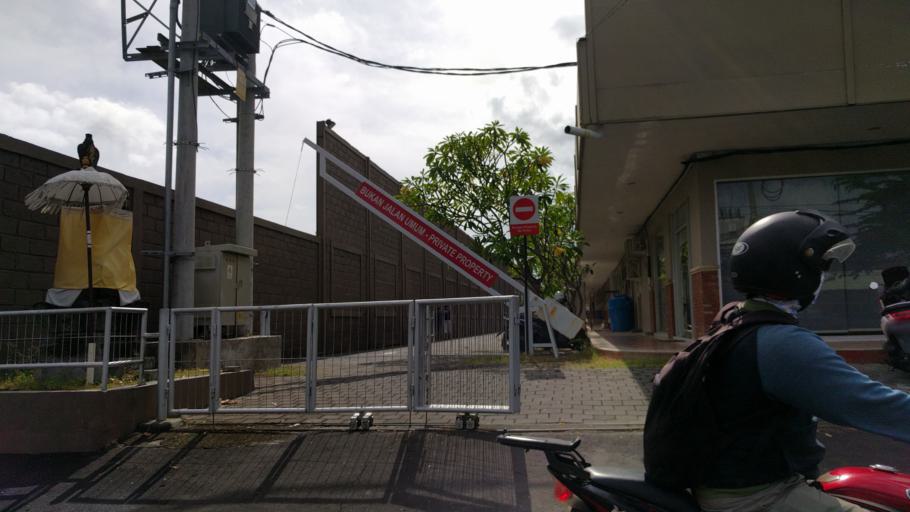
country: ID
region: Bali
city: Kuta
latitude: -8.6793
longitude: 115.1630
